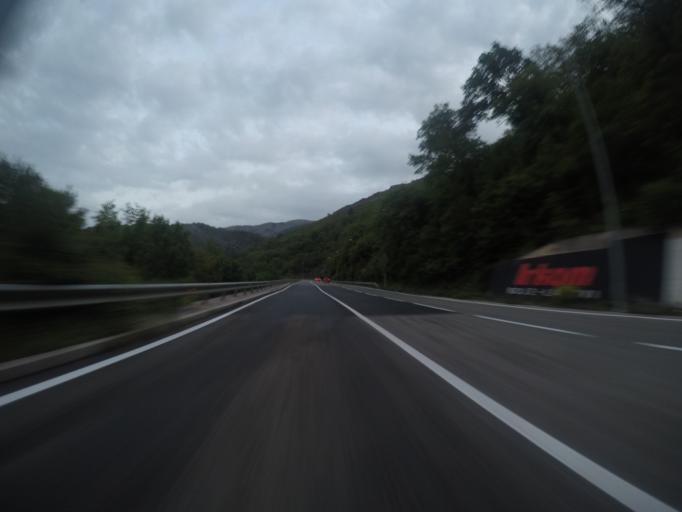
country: ME
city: Petrovac na Moru
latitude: 42.2066
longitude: 18.9497
